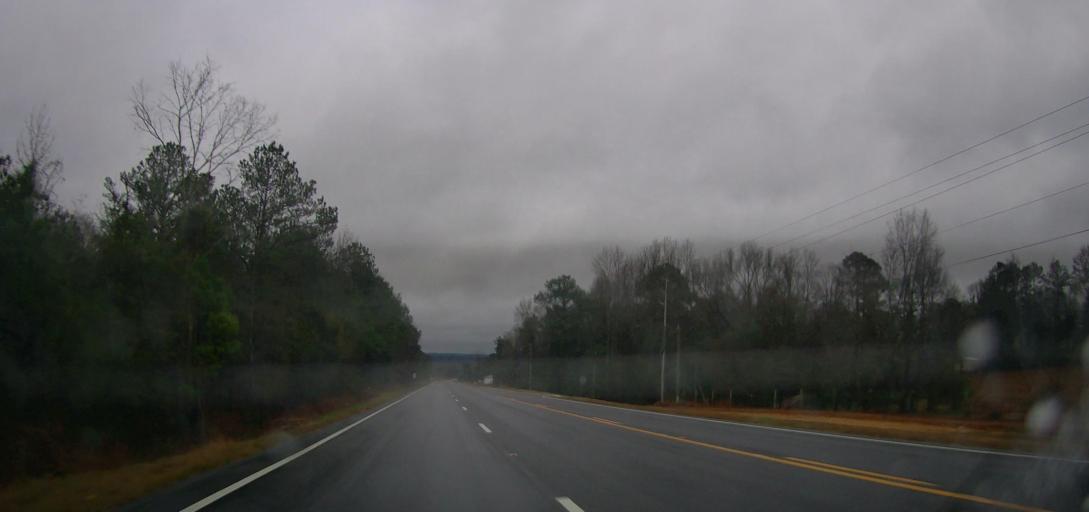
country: US
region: Alabama
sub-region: Chilton County
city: Thorsby
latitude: 32.7808
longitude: -86.8931
